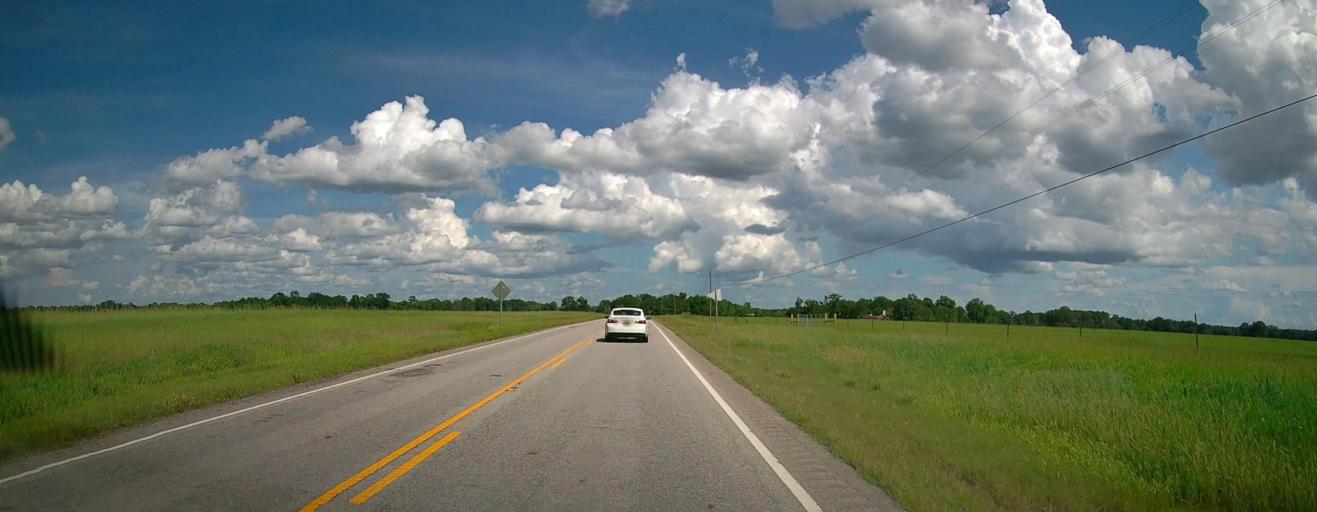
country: US
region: Alabama
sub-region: Lee County
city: Auburn
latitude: 32.4280
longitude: -85.4590
